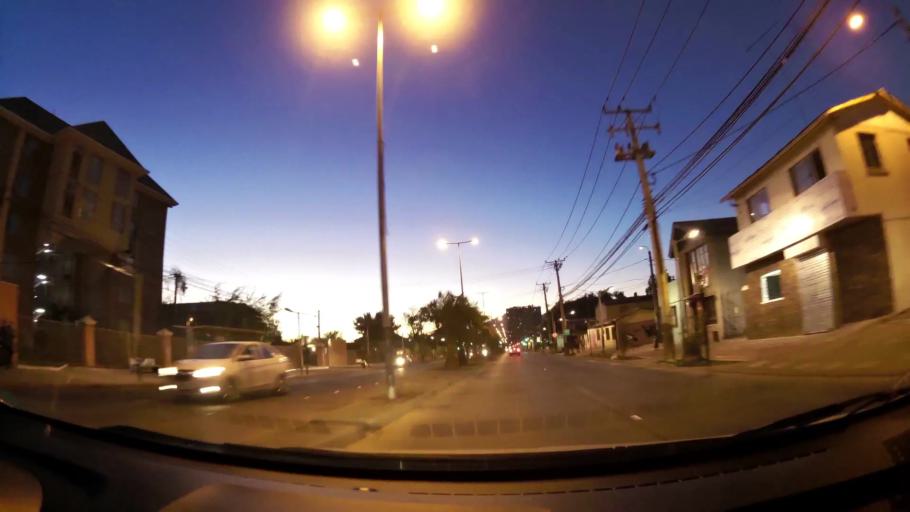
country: CL
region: O'Higgins
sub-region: Provincia de Cachapoal
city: Rancagua
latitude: -34.1720
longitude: -70.7288
